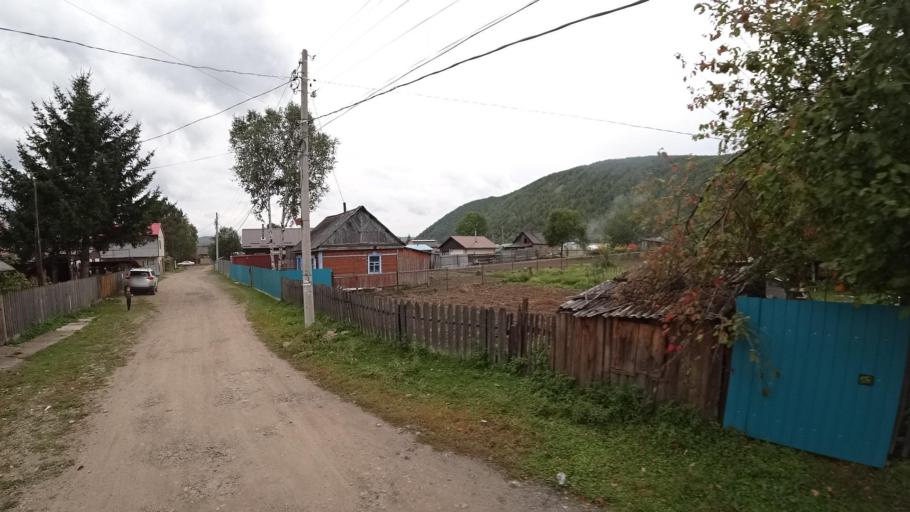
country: RU
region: Jewish Autonomous Oblast
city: Khingansk
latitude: 49.0055
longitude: 131.0493
